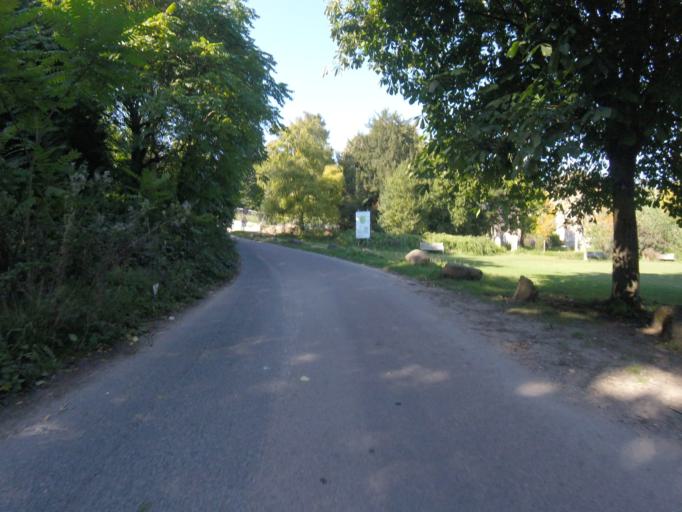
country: GB
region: England
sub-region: Brighton and Hove
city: Brighton
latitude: 50.8698
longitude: -0.1022
